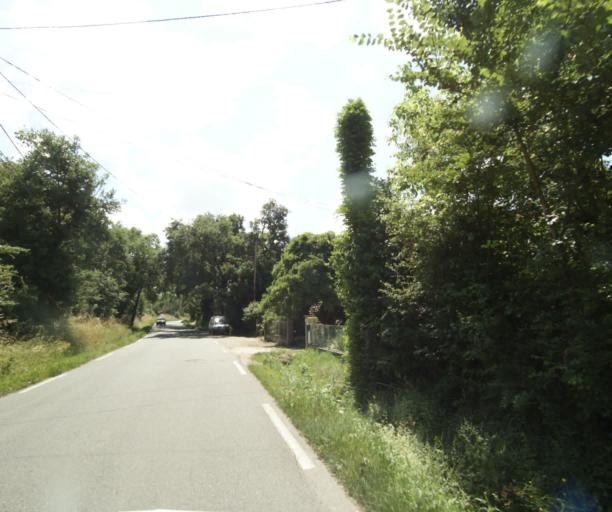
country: FR
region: Midi-Pyrenees
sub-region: Departement du Tarn-et-Garonne
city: Montauban
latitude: 44.0388
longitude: 1.3489
